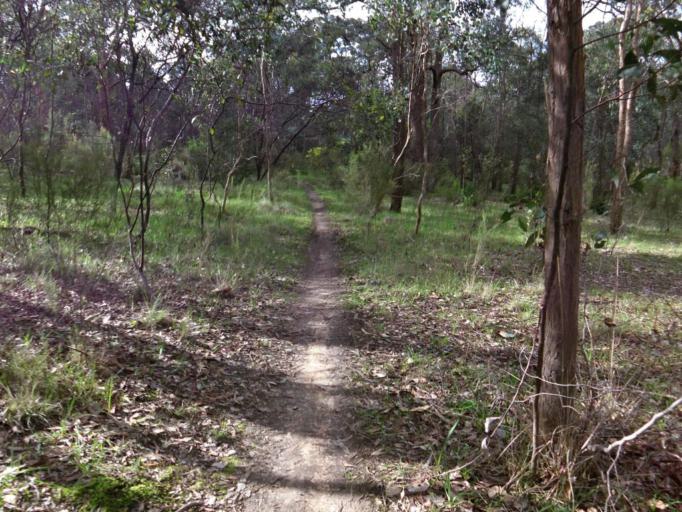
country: AU
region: Victoria
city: Plenty
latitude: -37.6693
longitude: 145.1057
